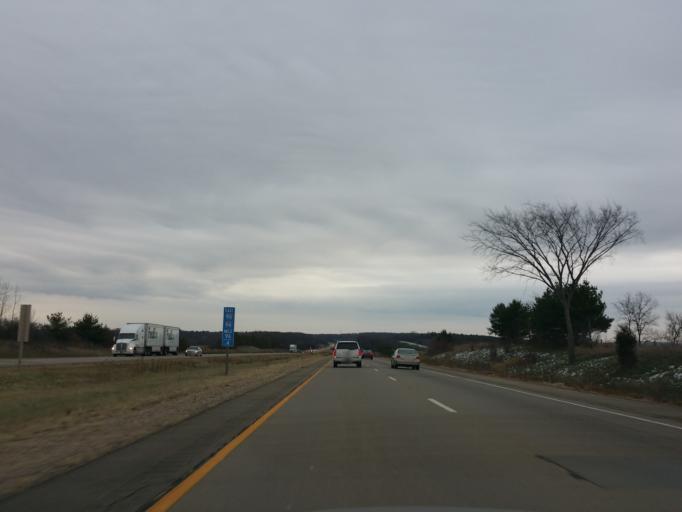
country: US
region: Wisconsin
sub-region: Sauk County
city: Baraboo
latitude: 43.5569
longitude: -89.7089
